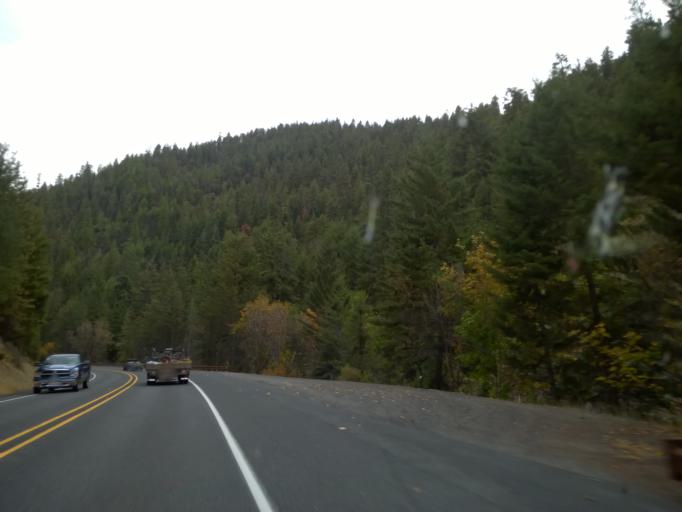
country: US
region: Washington
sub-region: Chelan County
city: Leavenworth
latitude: 47.4412
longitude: -120.6627
